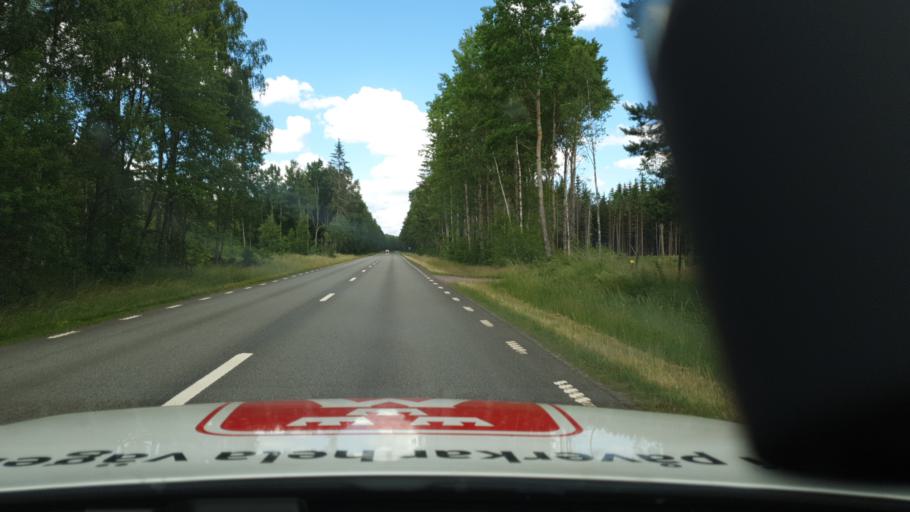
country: SE
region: Vaestra Goetaland
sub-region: Karlsborgs Kommun
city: Molltorp
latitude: 58.3967
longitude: 14.3570
